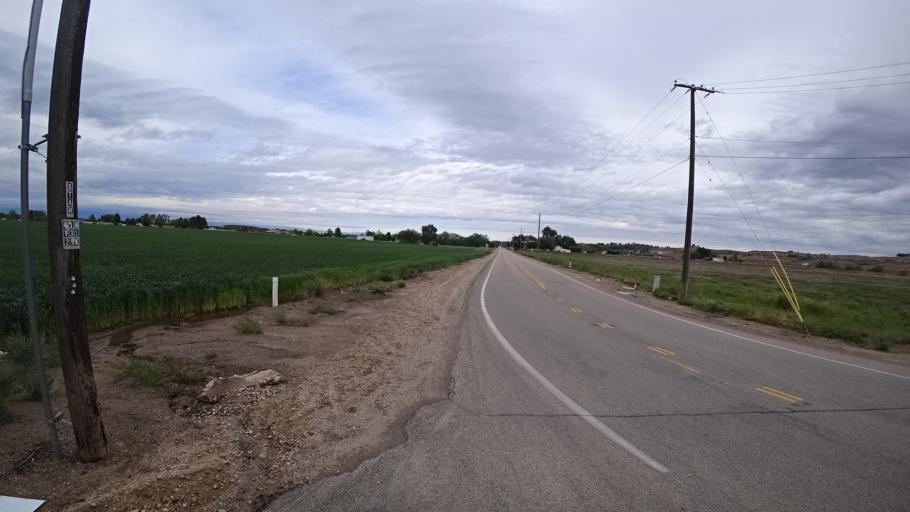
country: US
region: Idaho
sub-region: Ada County
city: Star
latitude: 43.7174
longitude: -116.4832
